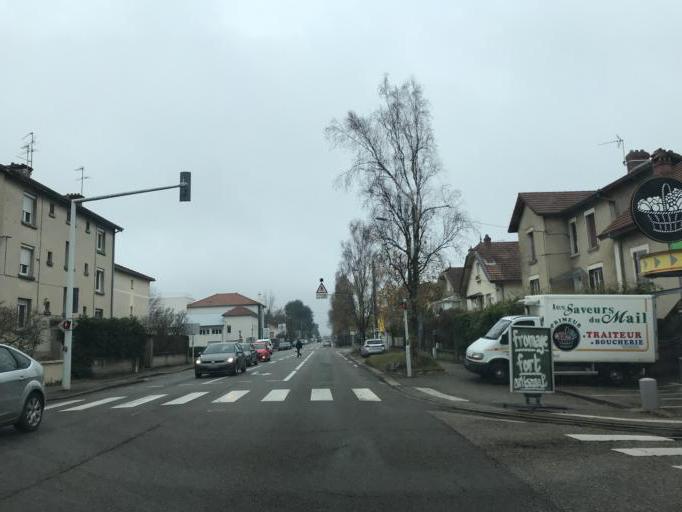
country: FR
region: Rhone-Alpes
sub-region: Departement de l'Ain
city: Peronnas
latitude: 46.2019
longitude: 5.2100
